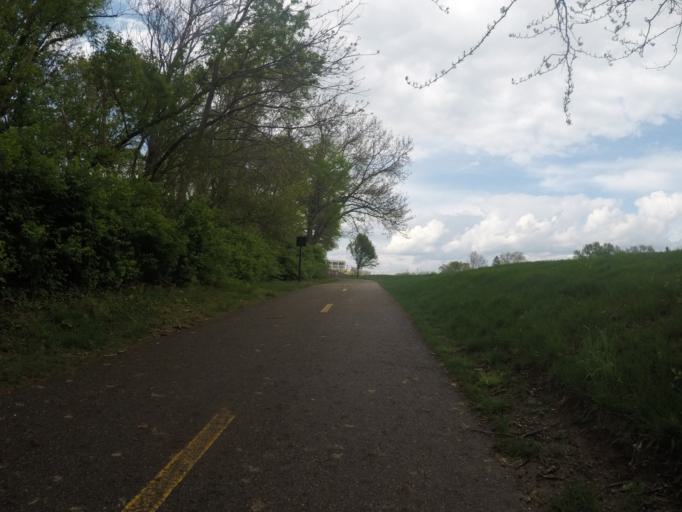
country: US
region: Ohio
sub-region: Franklin County
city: Grandview Heights
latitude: 39.9843
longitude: -83.0204
